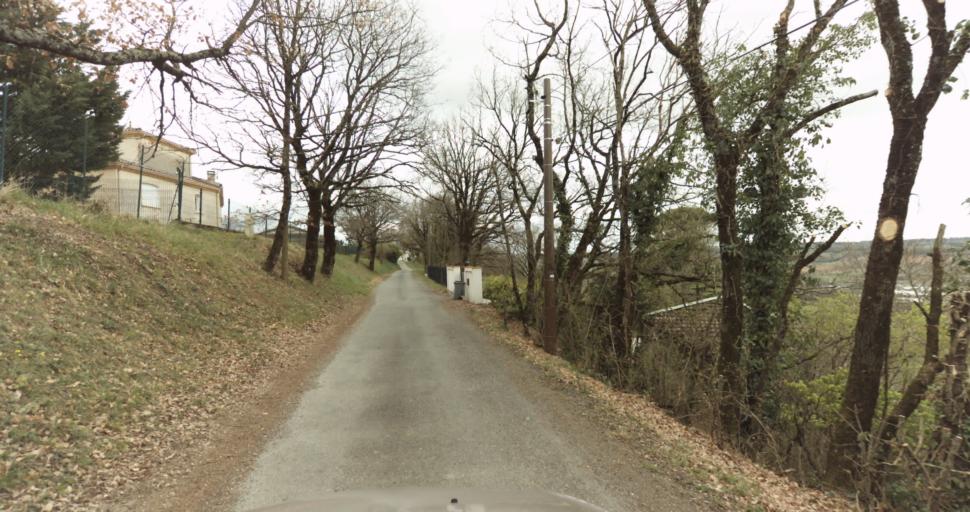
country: FR
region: Midi-Pyrenees
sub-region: Departement du Tarn
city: Puygouzon
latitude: 43.9010
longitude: 2.1657
